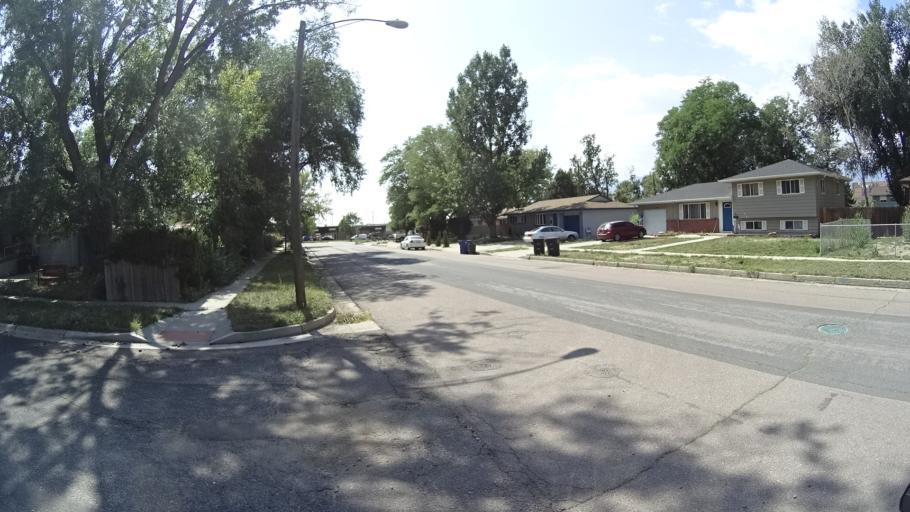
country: US
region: Colorado
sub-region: El Paso County
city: Colorado Springs
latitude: 38.8282
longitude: -104.7787
